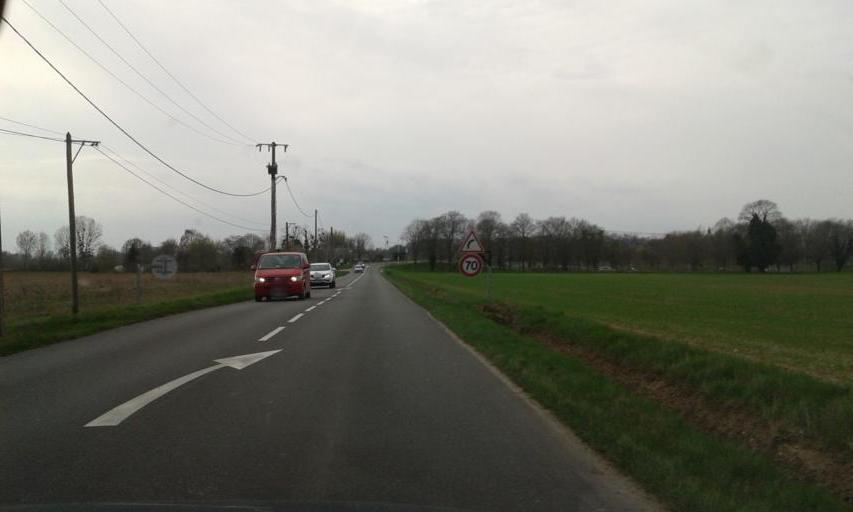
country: FR
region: Centre
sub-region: Departement du Loiret
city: Meung-sur-Loire
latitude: 47.8222
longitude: 1.7077
